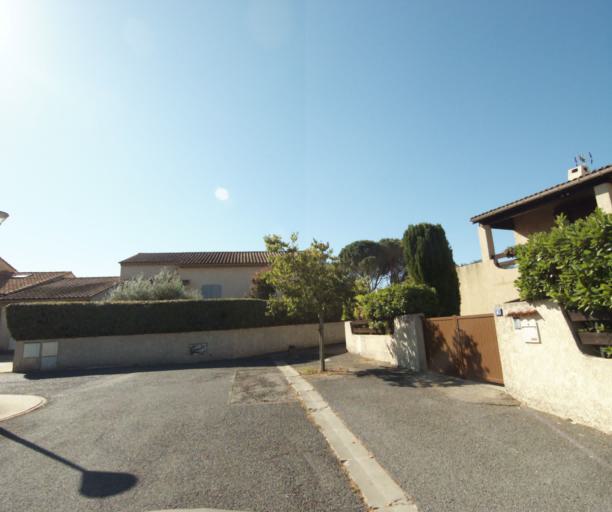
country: FR
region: Languedoc-Roussillon
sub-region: Departement du Gard
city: Bouillargues
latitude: 43.7998
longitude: 4.4193
